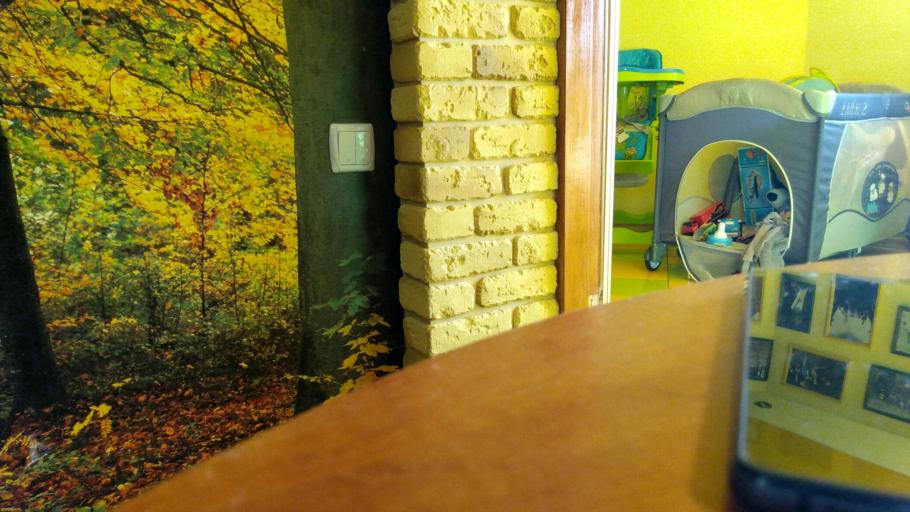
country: RU
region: Tverskaya
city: Likhoslavl'
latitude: 57.2140
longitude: 35.4934
